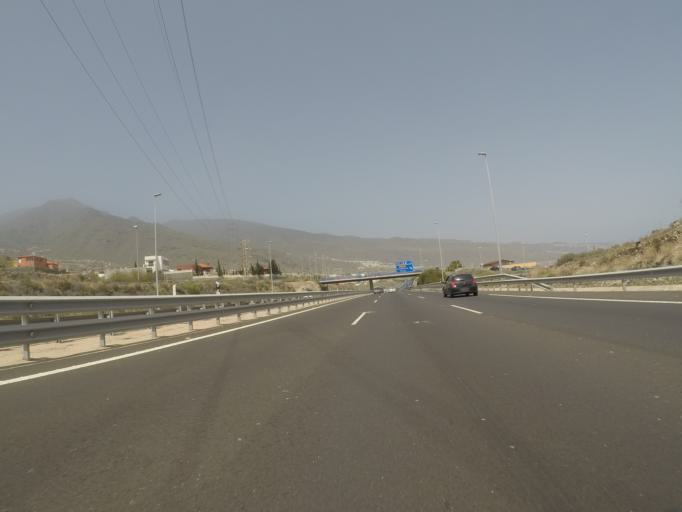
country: ES
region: Canary Islands
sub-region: Provincia de Santa Cruz de Tenerife
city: Candelaria
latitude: 28.3492
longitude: -16.3734
